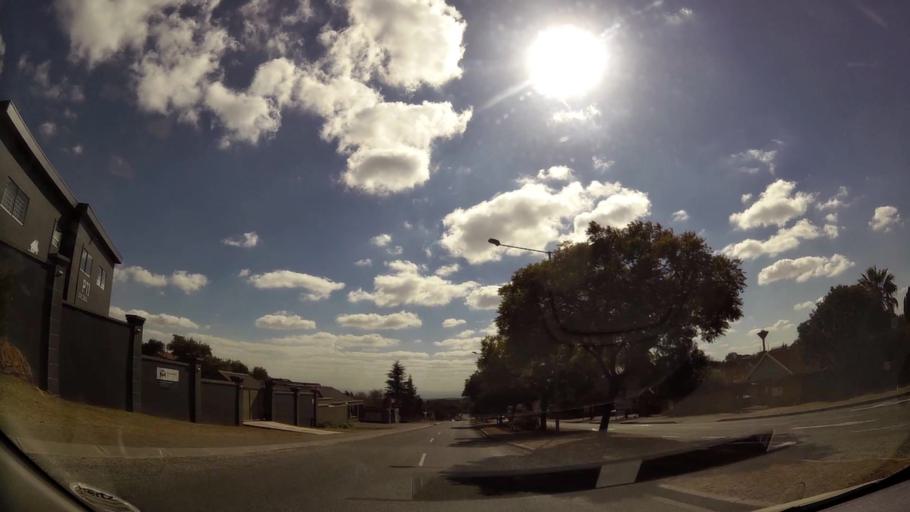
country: ZA
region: Gauteng
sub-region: West Rand District Municipality
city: Krugersdorp
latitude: -26.1002
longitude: 27.8042
